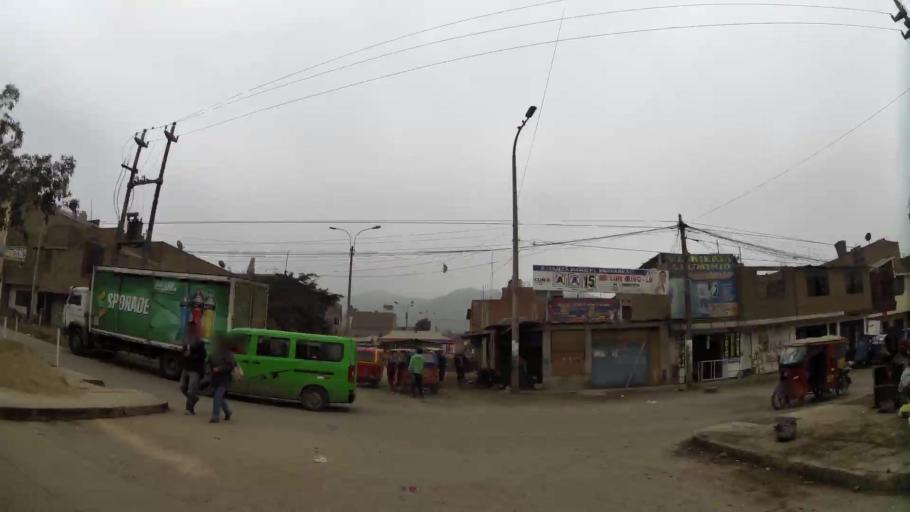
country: PE
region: Lima
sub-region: Lima
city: Independencia
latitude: -11.9435
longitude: -76.9911
